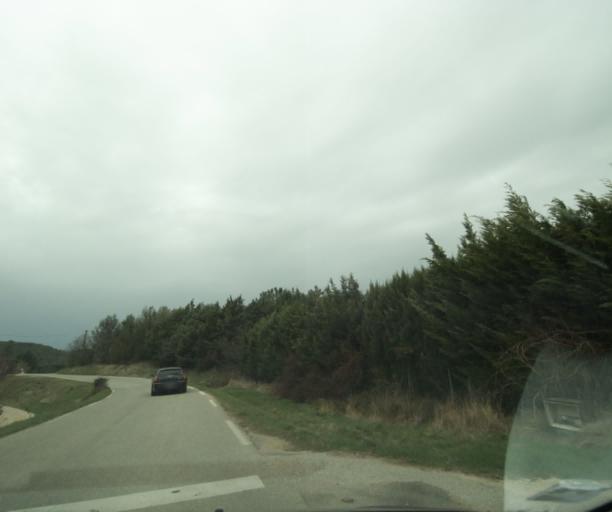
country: FR
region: Provence-Alpes-Cote d'Azur
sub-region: Departement des Bouches-du-Rhone
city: Saint-Marc-Jaumegarde
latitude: 43.5552
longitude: 5.5754
